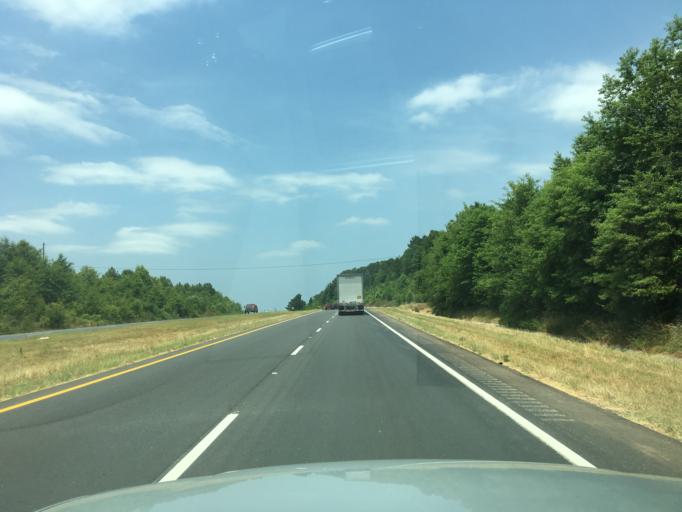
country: US
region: Georgia
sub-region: Jackson County
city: Commerce
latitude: 34.2289
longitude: -83.4503
